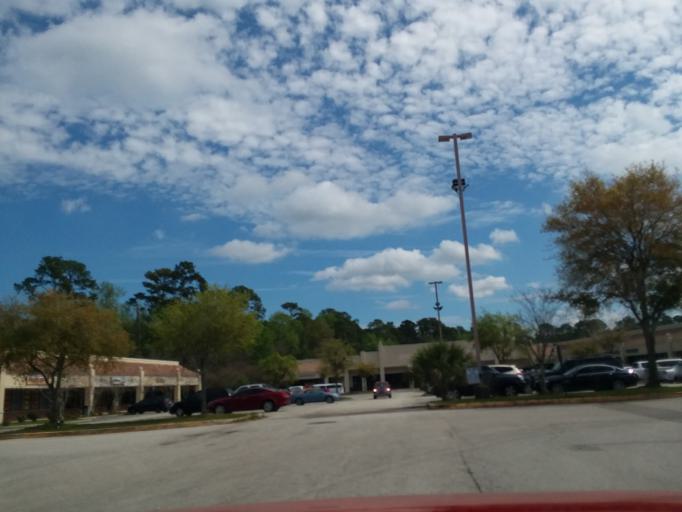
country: US
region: Florida
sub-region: Saint Johns County
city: Fruit Cove
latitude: 30.1871
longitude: -81.6270
